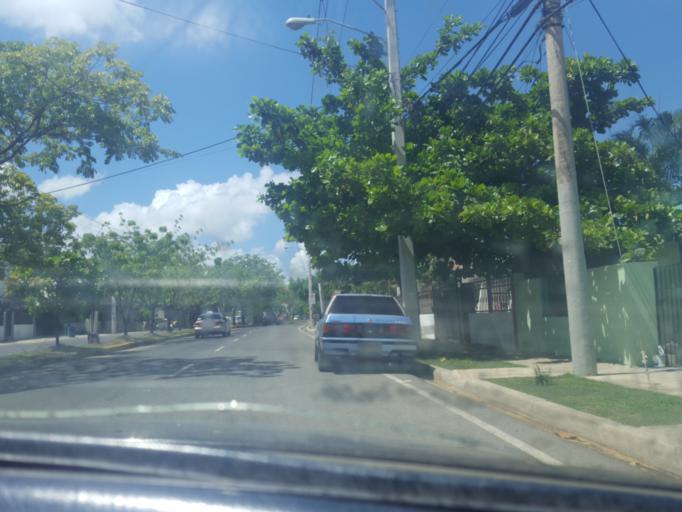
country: DO
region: Santiago
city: Santiago de los Caballeros
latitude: 19.4937
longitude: -70.7032
